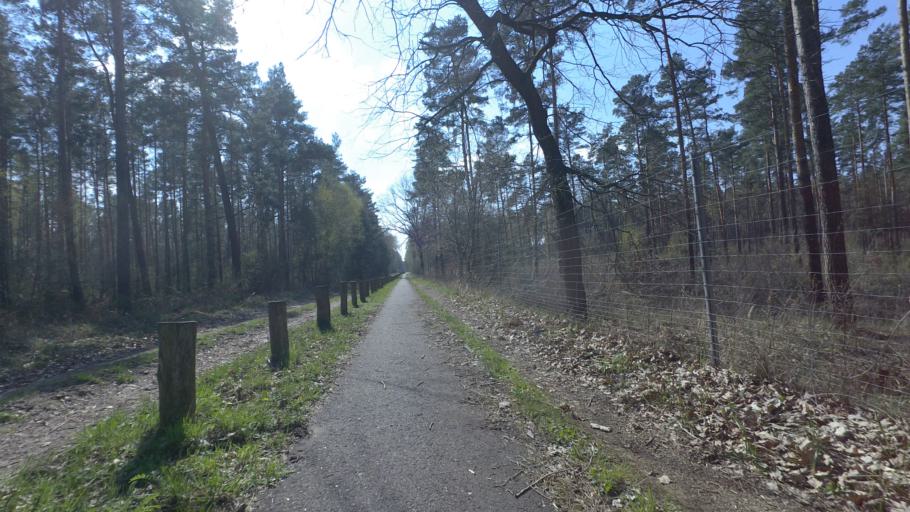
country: DE
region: Brandenburg
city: Mittenwalde
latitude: 52.1991
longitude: 13.5424
